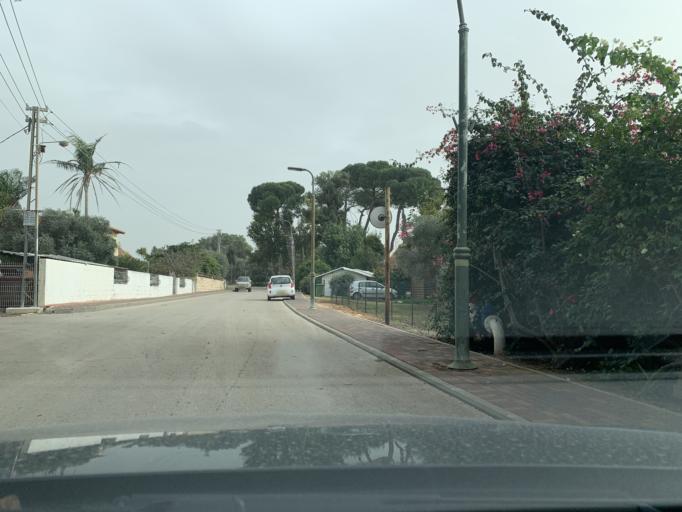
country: IL
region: Central District
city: Jaljulya
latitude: 32.1615
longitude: 34.9424
